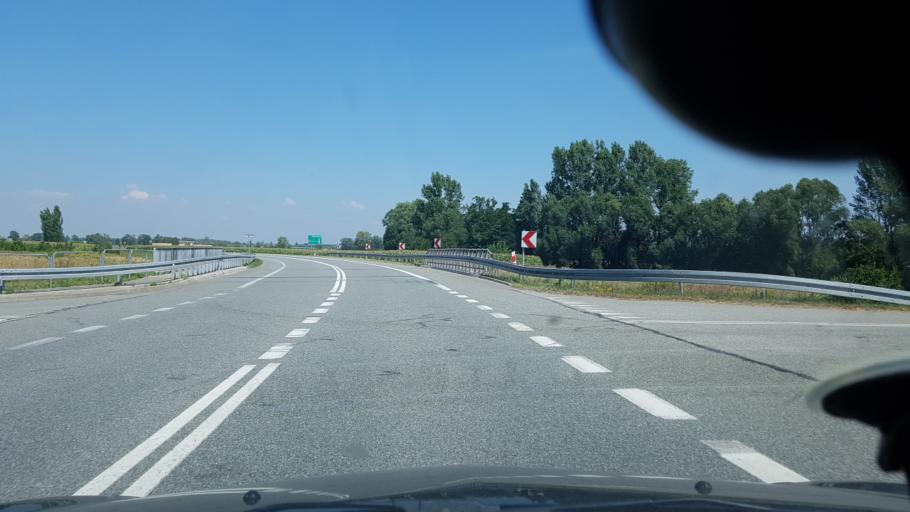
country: PL
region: Silesian Voivodeship
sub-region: Powiat raciborski
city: Chalupki
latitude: 49.9387
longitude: 18.3295
